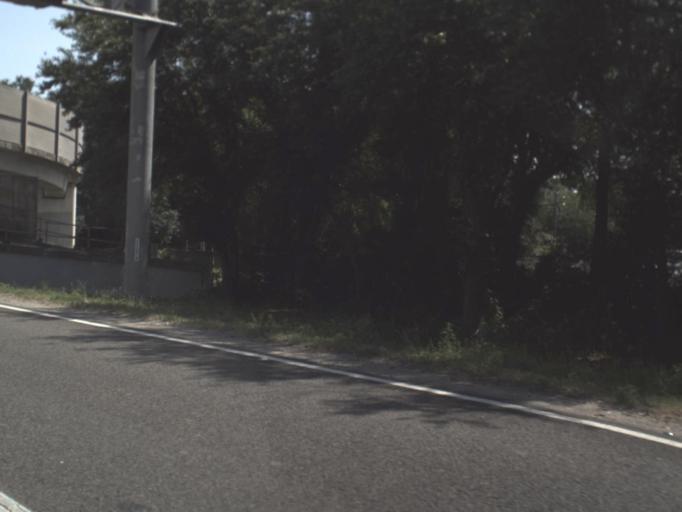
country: US
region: Florida
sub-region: Duval County
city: Jacksonville
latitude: 30.3398
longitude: -81.6680
